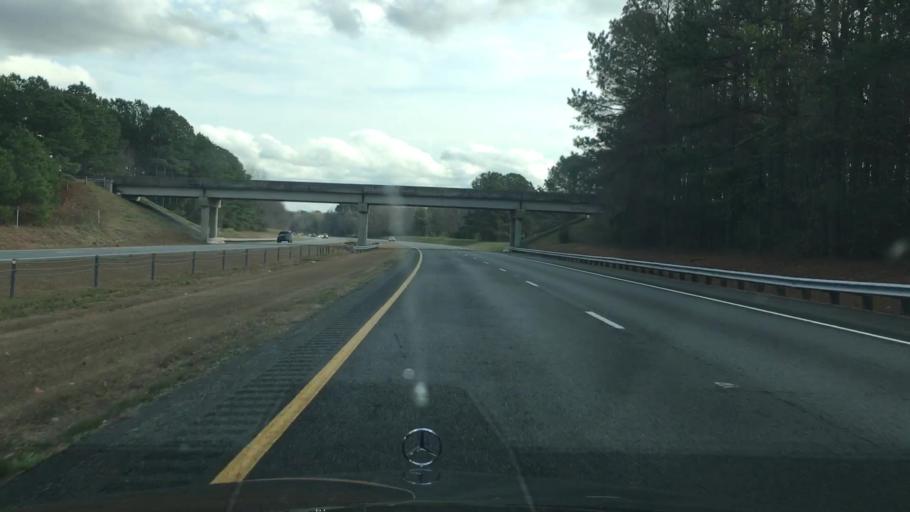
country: US
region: North Carolina
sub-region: Sampson County
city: Clinton
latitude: 35.2148
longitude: -78.3295
